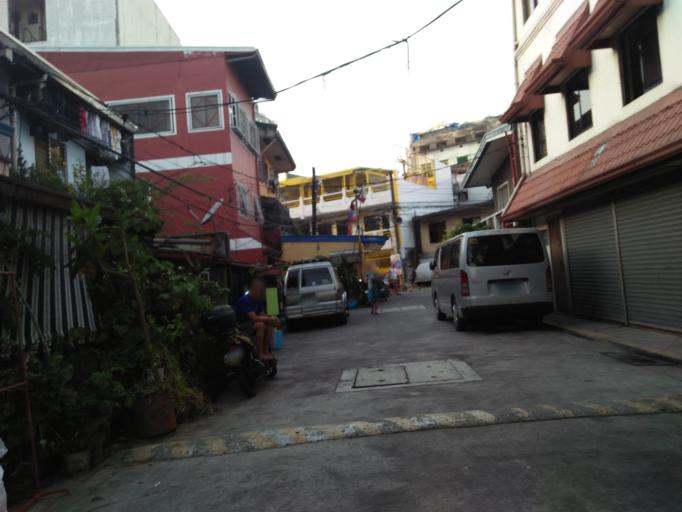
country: PH
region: Metro Manila
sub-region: San Juan
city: San Juan
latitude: 14.6017
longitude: 121.0167
